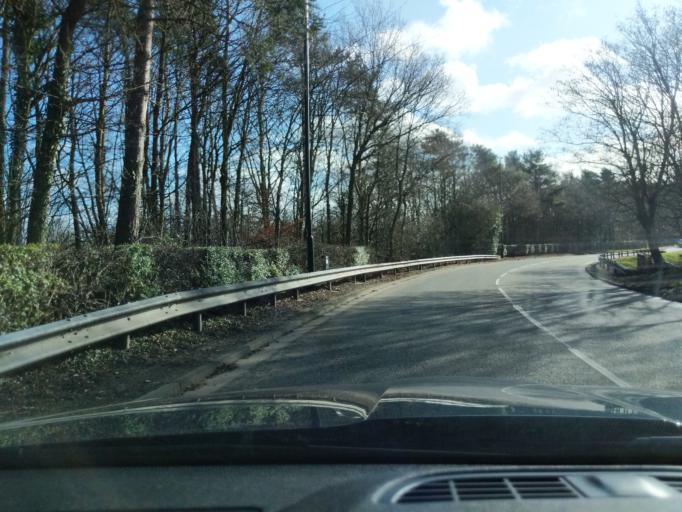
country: GB
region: England
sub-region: Sunderland
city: Washington
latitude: 54.8828
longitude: -1.5436
